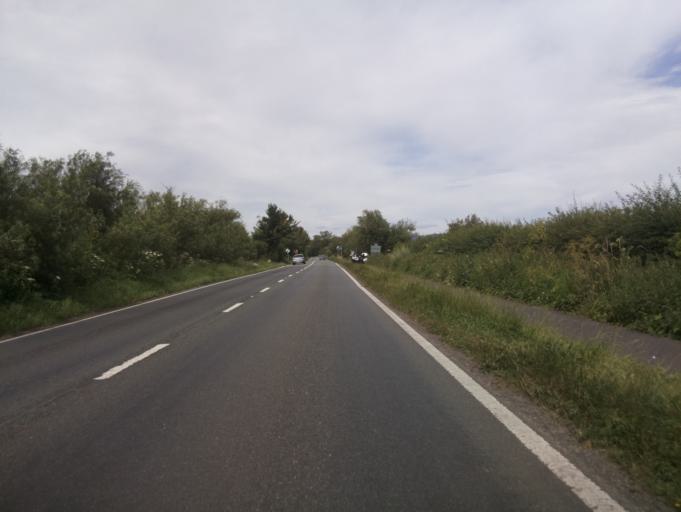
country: GB
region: England
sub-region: Somerset
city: Glastonbury
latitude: 51.1652
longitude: -2.6989
